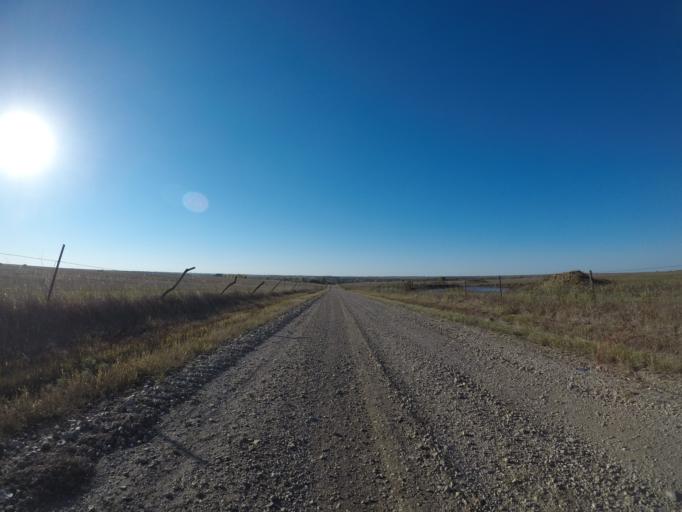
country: US
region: Kansas
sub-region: Wabaunsee County
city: Alma
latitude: 38.9337
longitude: -96.4641
